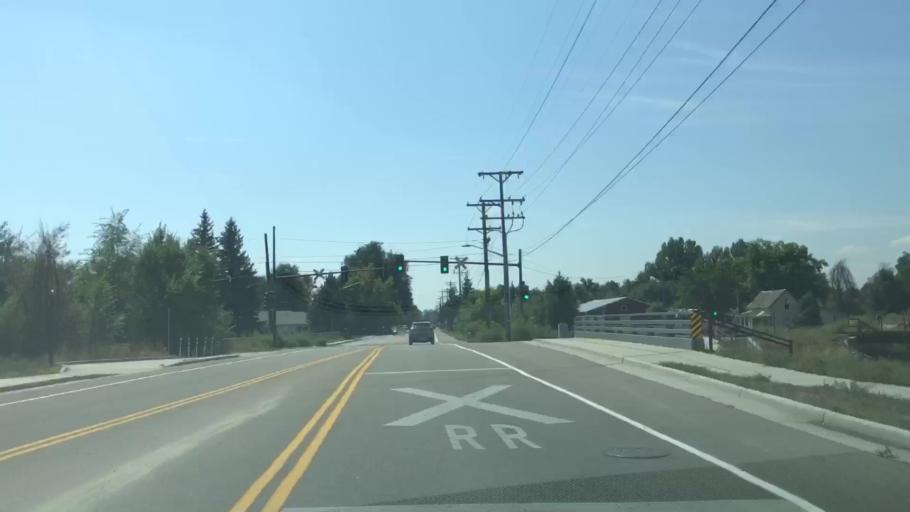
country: US
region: Colorado
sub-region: Larimer County
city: Loveland
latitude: 40.4008
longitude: -105.0589
